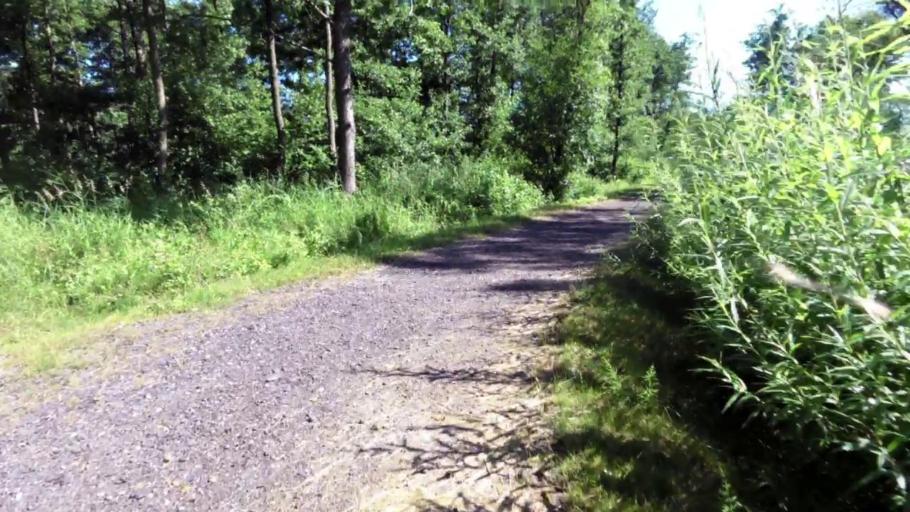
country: PL
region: West Pomeranian Voivodeship
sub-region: Powiat koszalinski
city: Mielno
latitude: 54.2781
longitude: 16.1222
